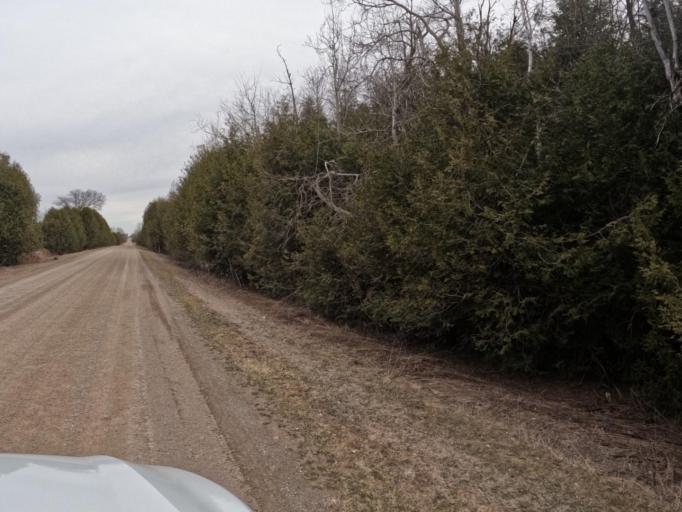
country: CA
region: Ontario
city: Shelburne
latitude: 43.9308
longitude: -80.2578
